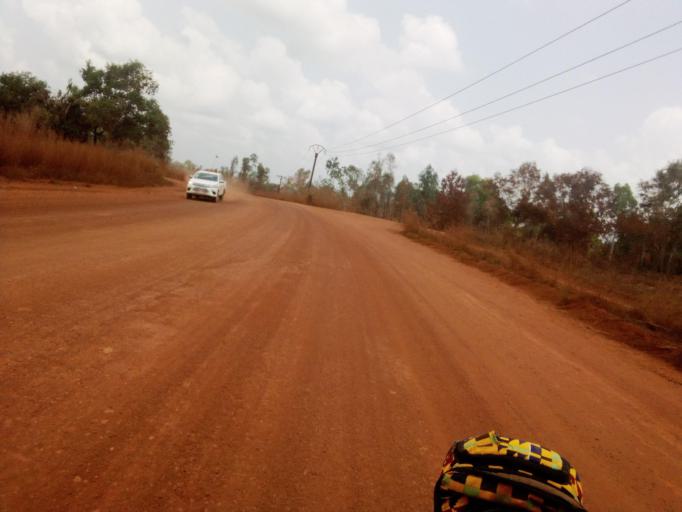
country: SL
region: Southern Province
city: Mogbwemo
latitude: 7.7540
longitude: -12.2937
